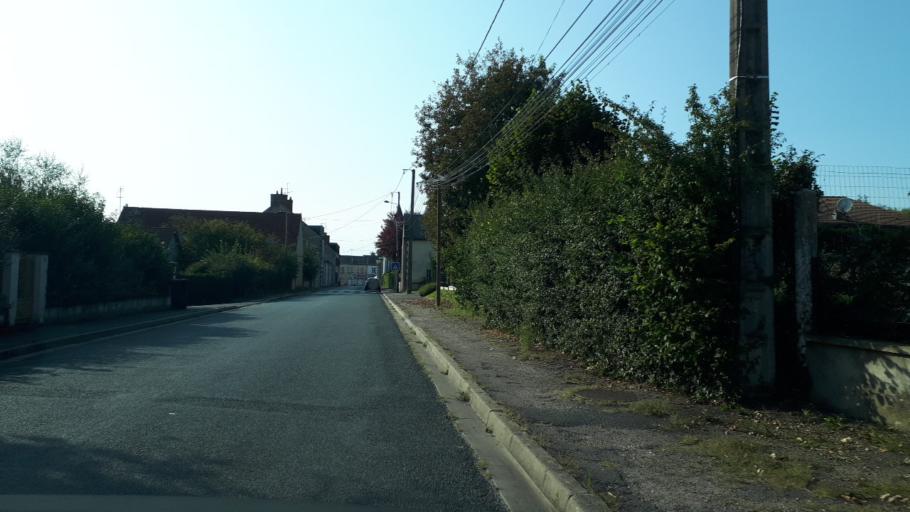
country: FR
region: Centre
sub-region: Departement du Cher
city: Saint-Eloy-de-Gy
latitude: 47.2244
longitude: 2.3217
